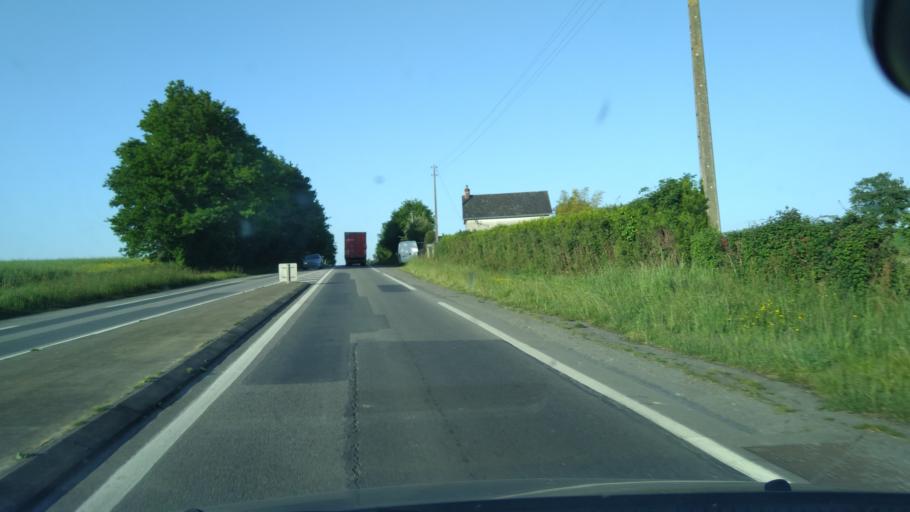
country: FR
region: Pays de la Loire
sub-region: Departement de la Mayenne
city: Renaze
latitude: 47.8030
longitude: -1.0439
